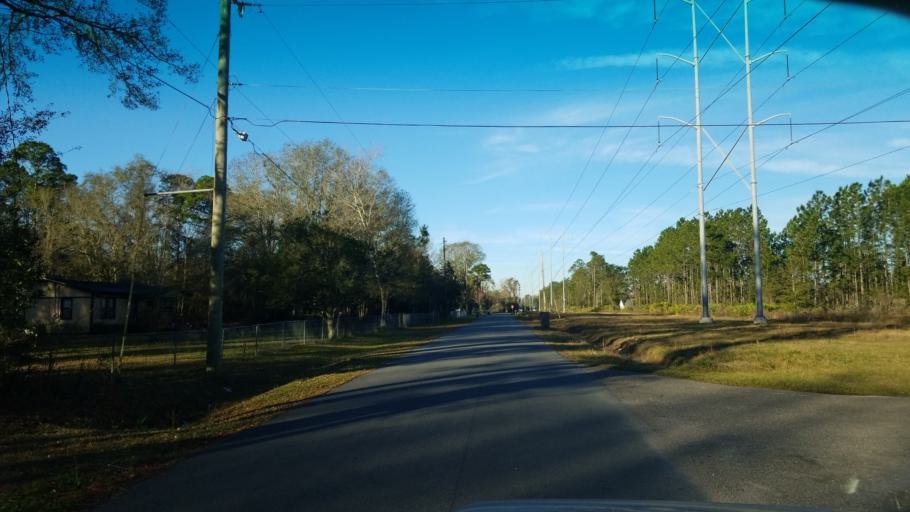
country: US
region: Florida
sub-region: Duval County
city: Baldwin
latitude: 30.3236
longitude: -81.8454
